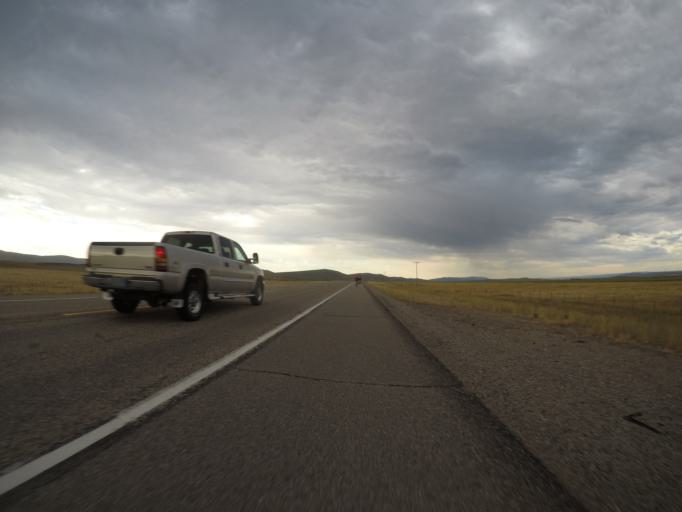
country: US
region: Utah
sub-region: Rich County
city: Randolph
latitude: 41.9169
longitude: -110.9550
